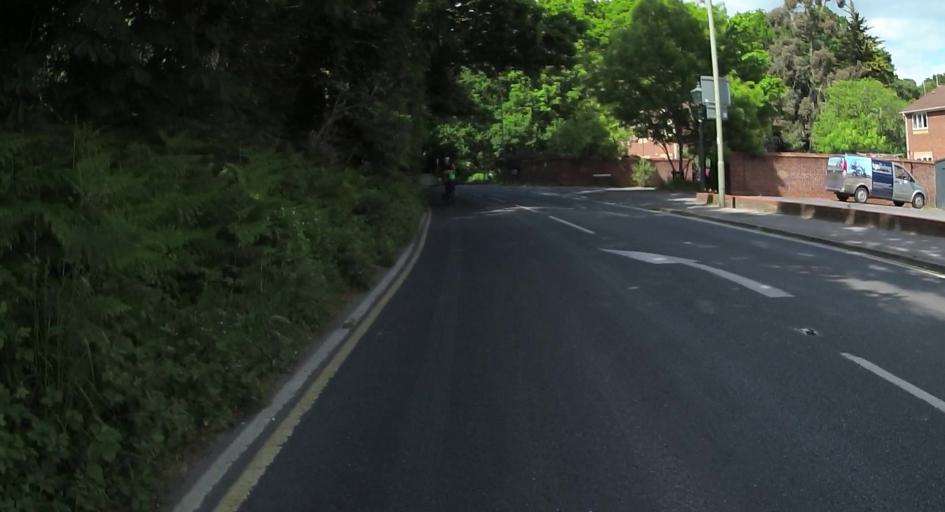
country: GB
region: England
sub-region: Surrey
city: Hale
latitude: 51.2398
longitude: -0.7863
